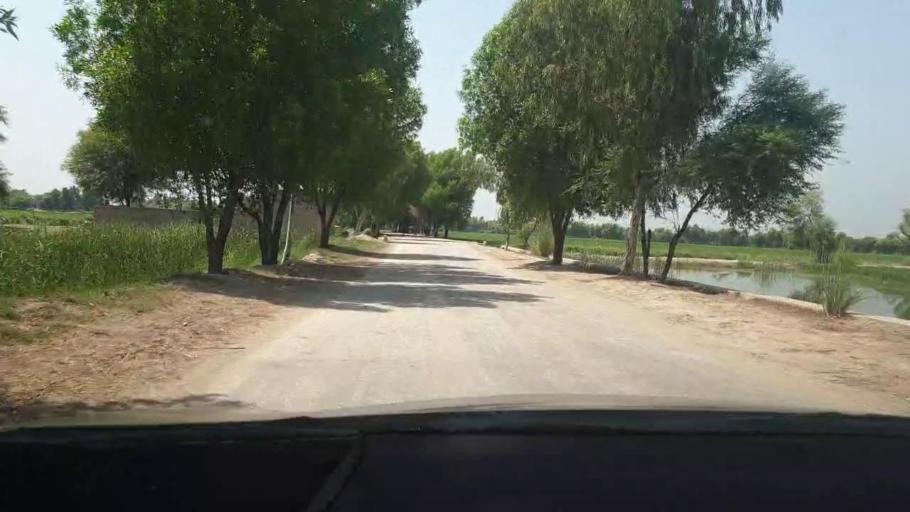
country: PK
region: Sindh
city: Miro Khan
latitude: 27.6719
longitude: 68.0544
